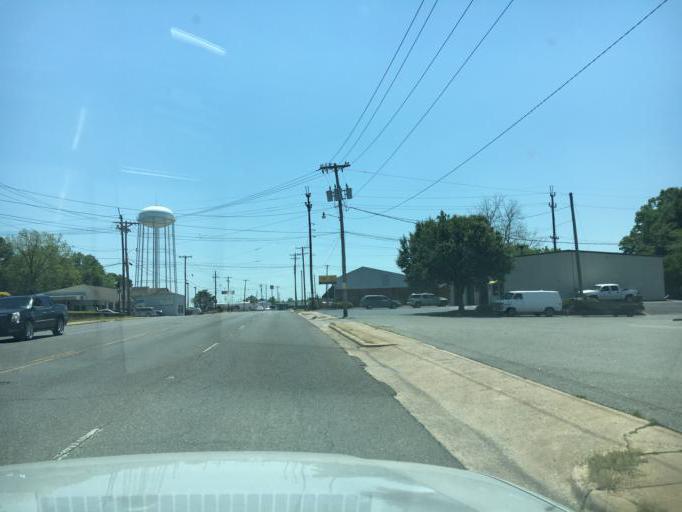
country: US
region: North Carolina
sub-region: Cleveland County
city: Shelby
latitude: 35.2835
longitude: -81.5409
